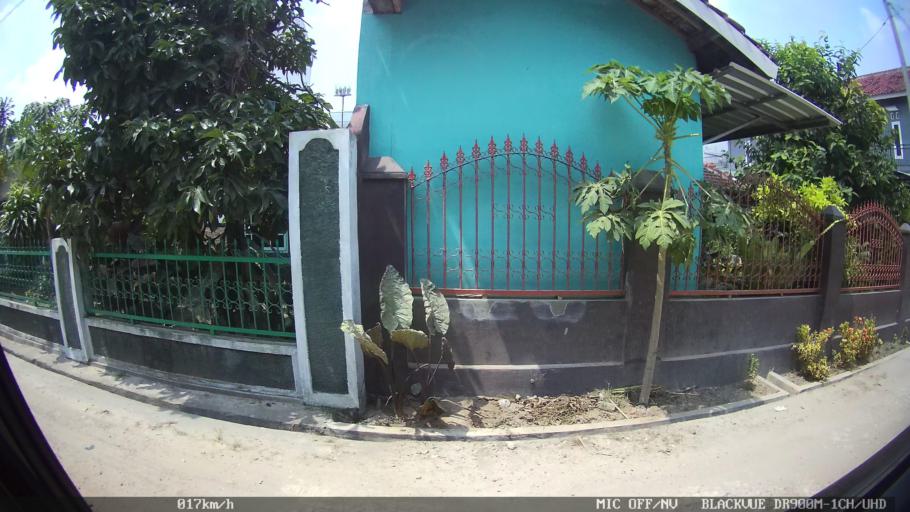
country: ID
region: Lampung
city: Pringsewu
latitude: -5.3573
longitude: 104.9803
